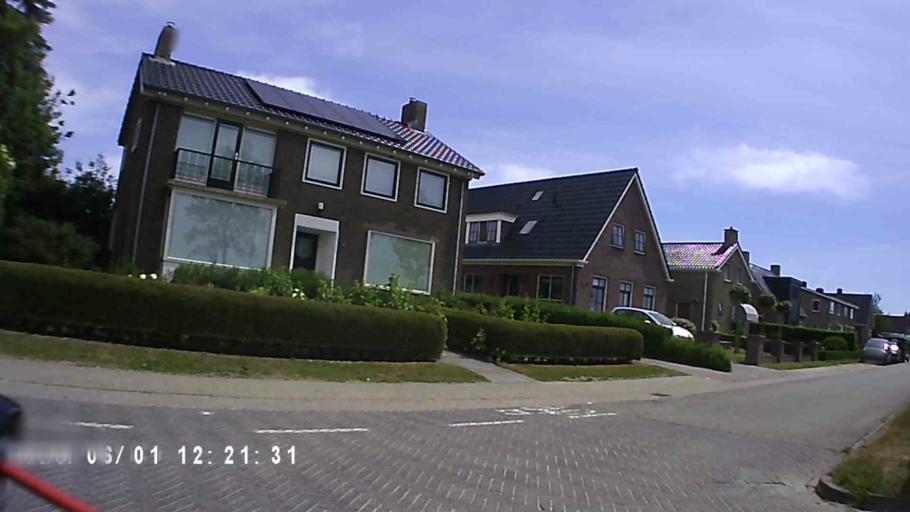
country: NL
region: Friesland
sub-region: Gemeente Harlingen
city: Harlingen
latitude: 53.1286
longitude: 5.4795
